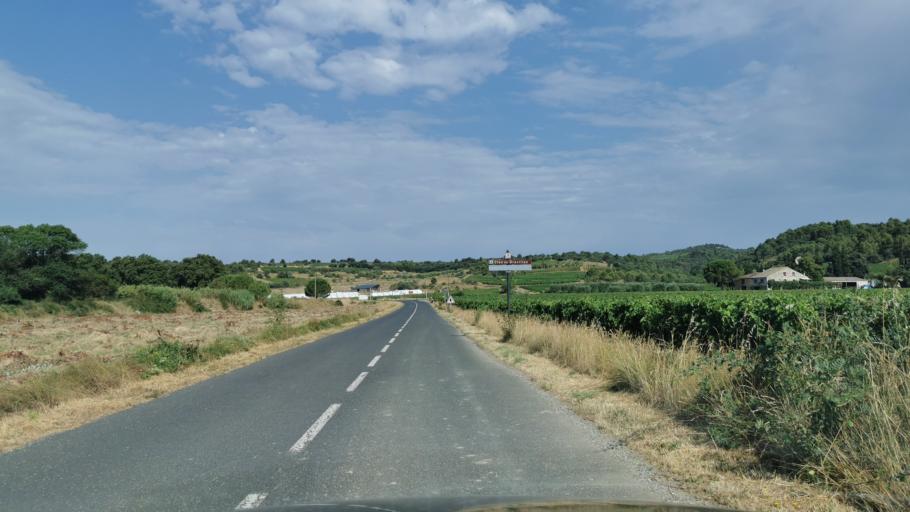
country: FR
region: Languedoc-Roussillon
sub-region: Departement de l'Aude
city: Bize-Minervois
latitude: 43.3446
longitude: 2.8635
